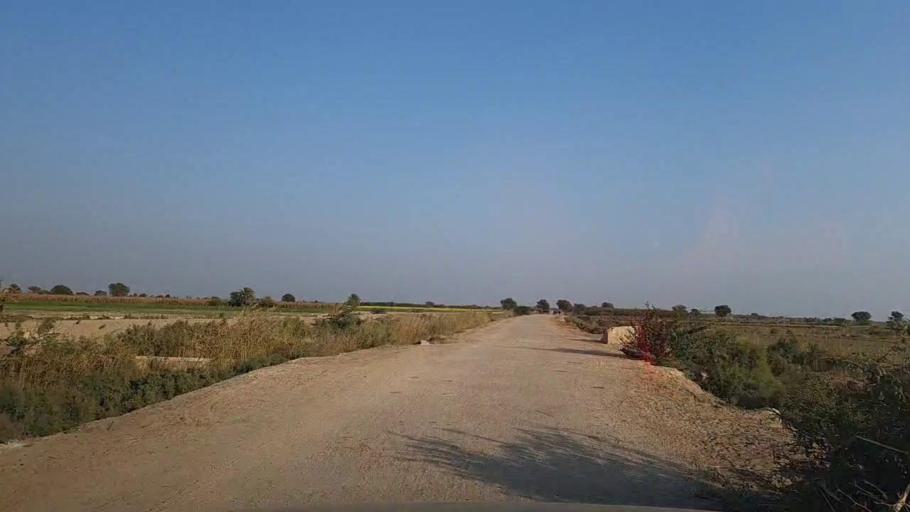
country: PK
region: Sindh
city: Tando Mittha Khan
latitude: 25.9397
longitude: 69.0803
